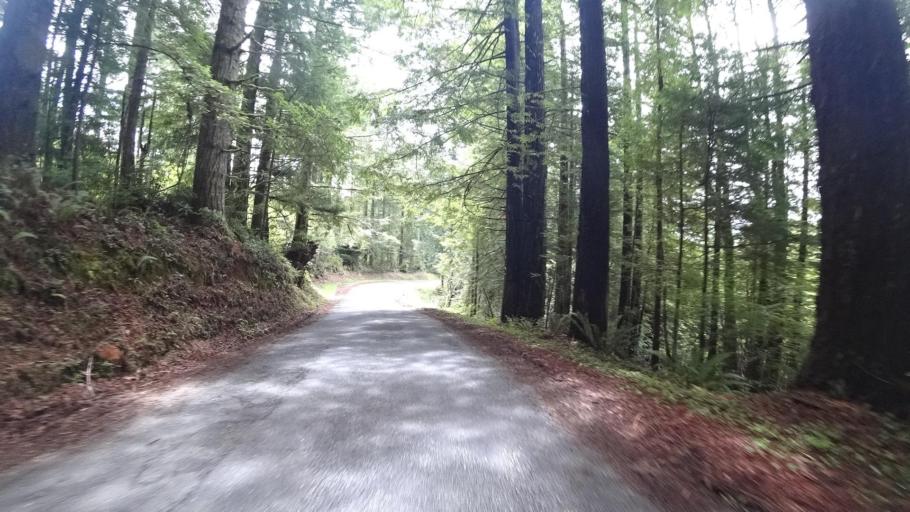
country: US
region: California
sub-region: Humboldt County
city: Bayside
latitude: 40.8300
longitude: -124.0126
